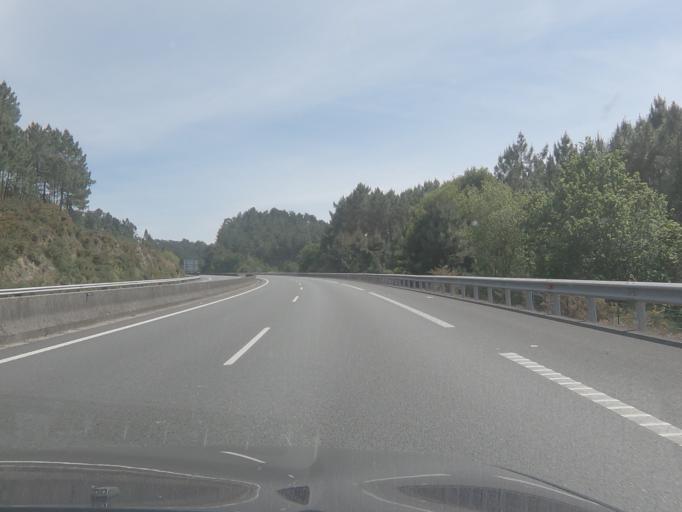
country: ES
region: Galicia
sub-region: Provincia de Pontevedra
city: Portas
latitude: 42.5834
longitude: -8.6759
